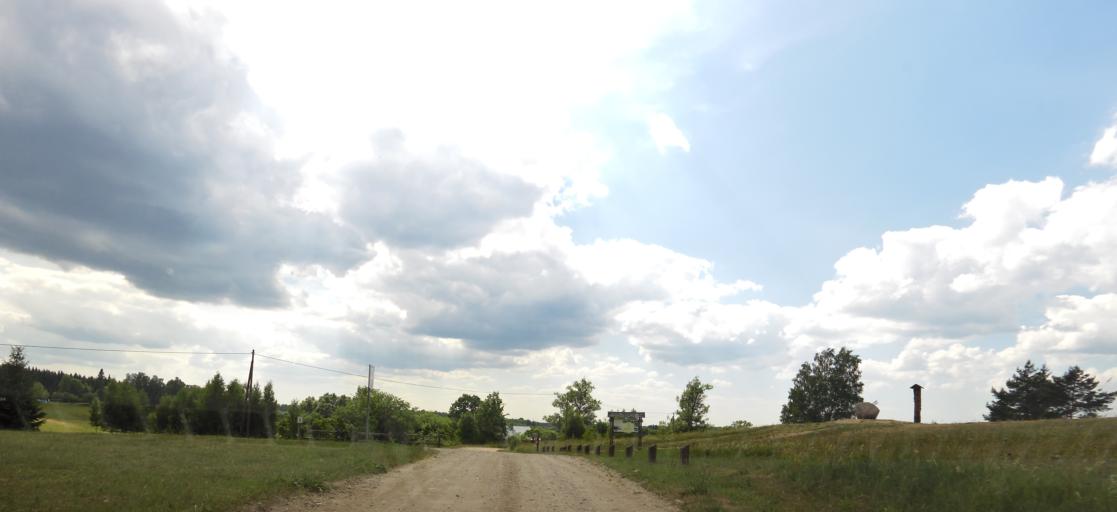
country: LT
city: Skaidiskes
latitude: 54.5308
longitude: 25.6279
